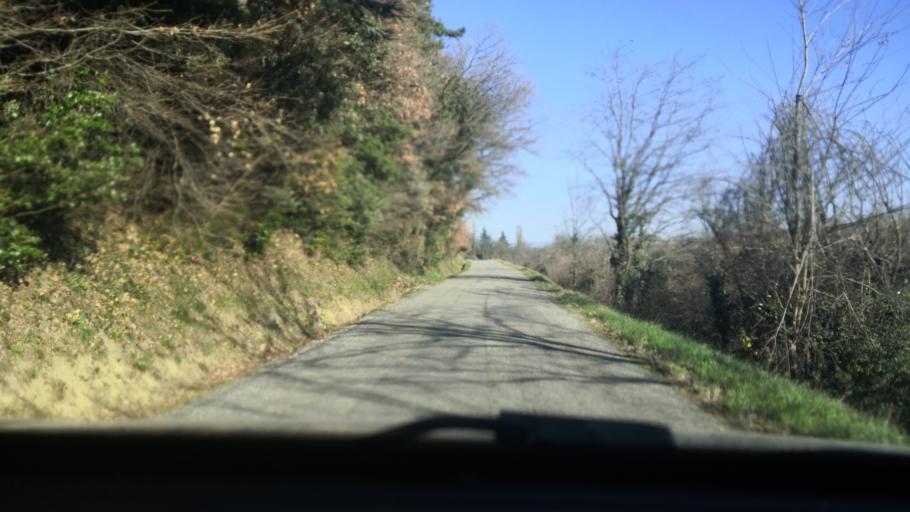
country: FR
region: Rhone-Alpes
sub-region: Departement de la Drome
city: Savasse
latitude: 44.6354
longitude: 4.7903
